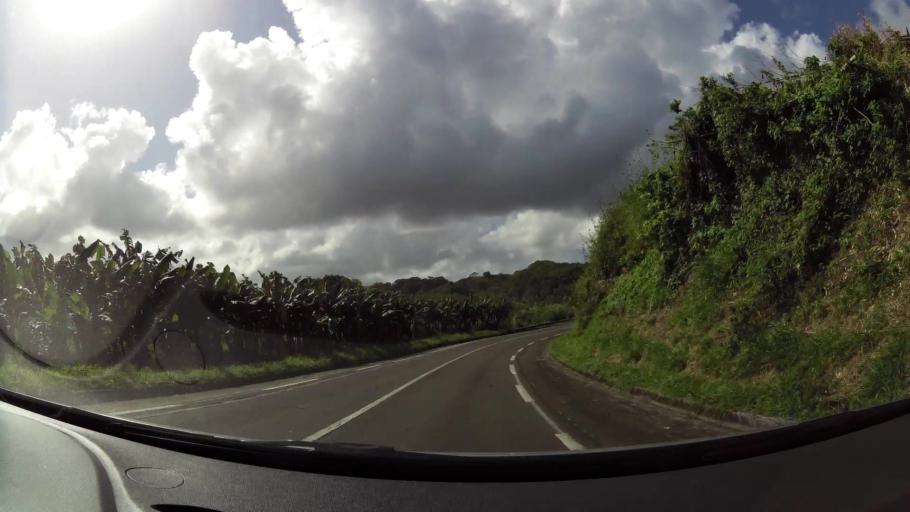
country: MQ
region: Martinique
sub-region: Martinique
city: Basse-Pointe
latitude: 14.8329
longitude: -61.0986
